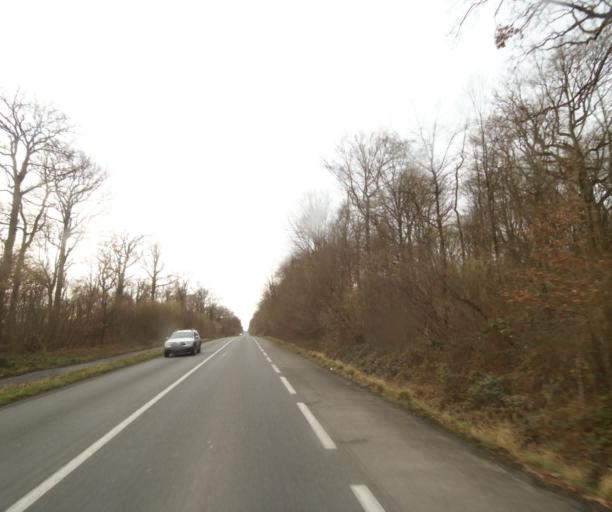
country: BE
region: Wallonia
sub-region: Province du Hainaut
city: Peruwelz
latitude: 50.4826
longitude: 3.6016
